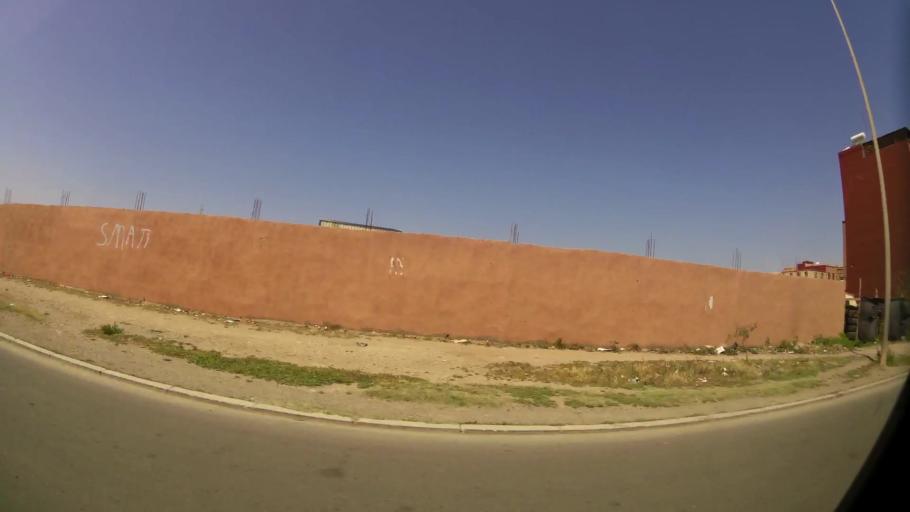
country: MA
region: Souss-Massa-Draa
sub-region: Inezgane-Ait Mellou
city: Inezgane
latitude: 30.3326
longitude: -9.5006
